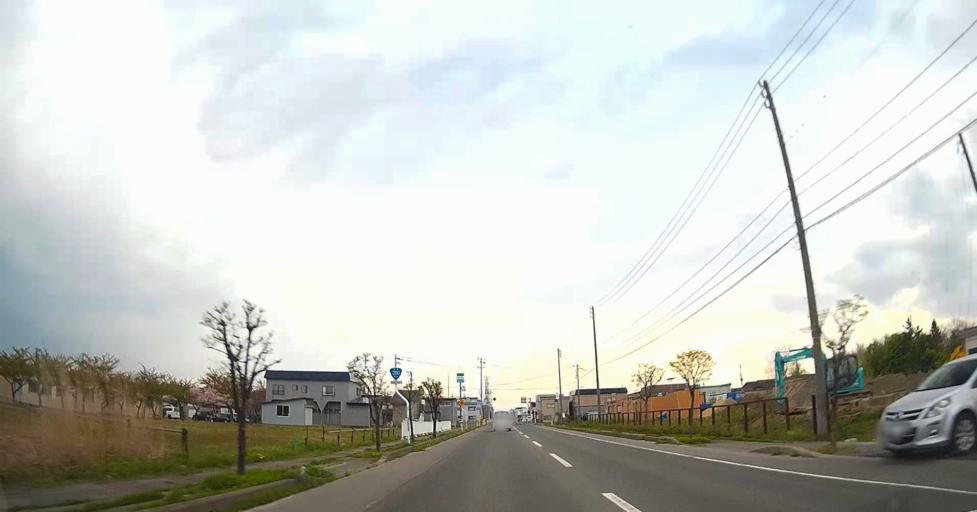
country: JP
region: Aomori
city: Aomori Shi
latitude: 40.8608
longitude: 140.6812
